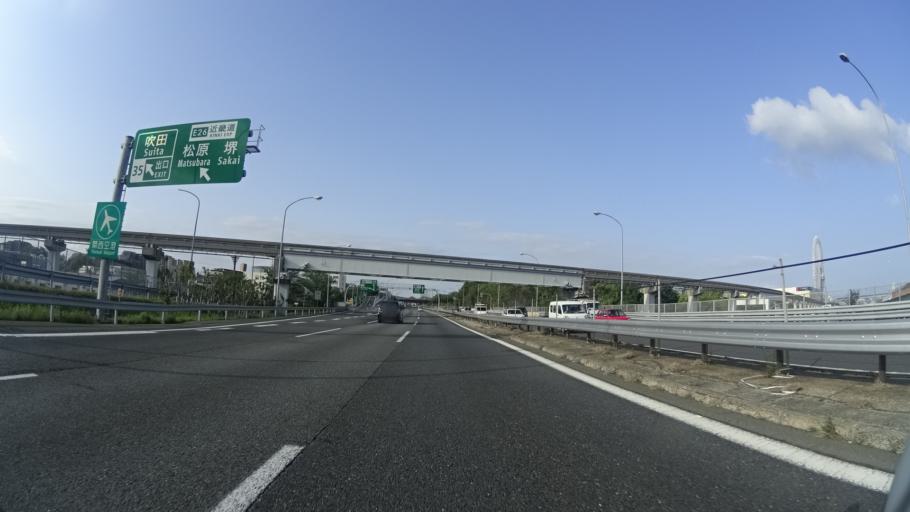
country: JP
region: Osaka
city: Ibaraki
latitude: 34.8081
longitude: 135.5439
